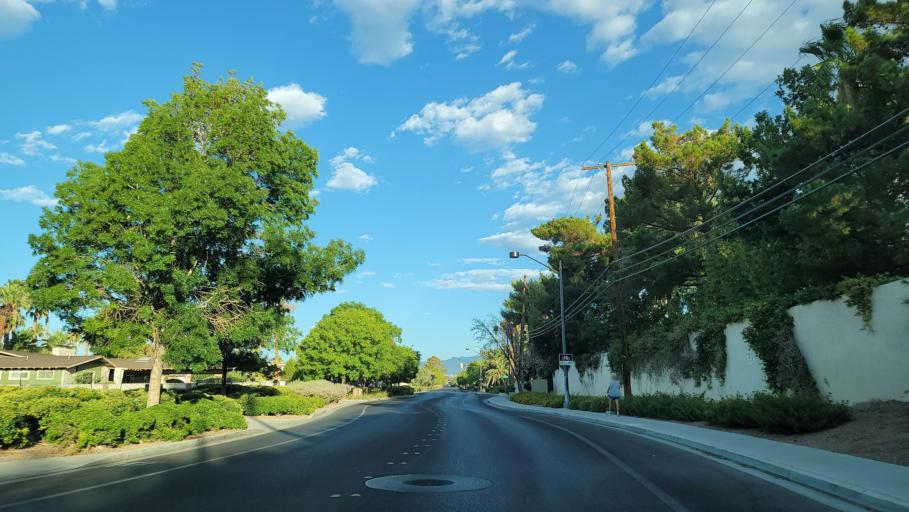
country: US
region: Nevada
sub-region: Clark County
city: Las Vegas
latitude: 36.1662
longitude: -115.1781
